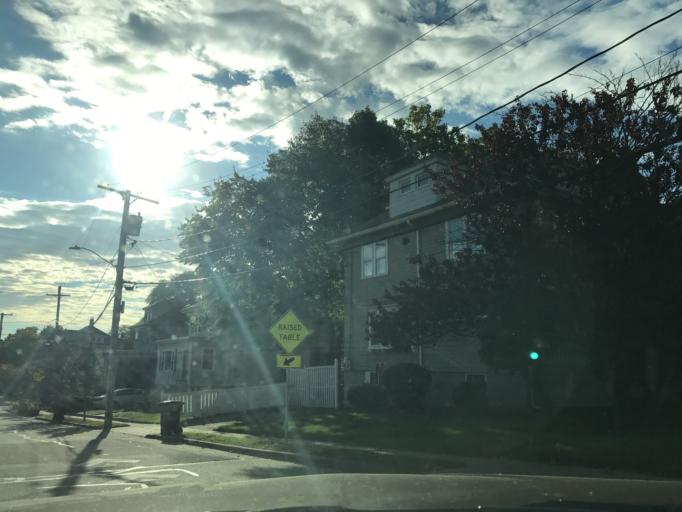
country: US
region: Massachusetts
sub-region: Middlesex County
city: Watertown
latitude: 42.3738
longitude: -71.1633
